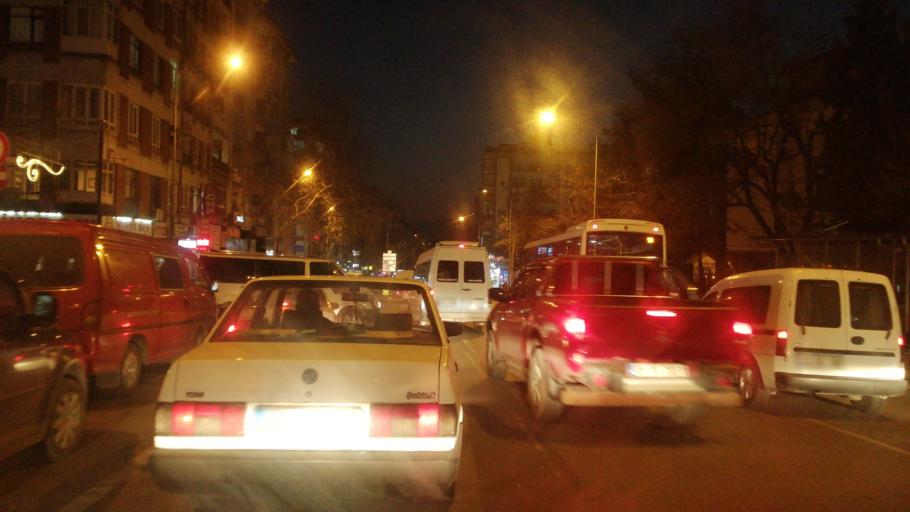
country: TR
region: Kahramanmaras
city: Kahramanmaras
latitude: 37.5796
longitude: 36.9308
